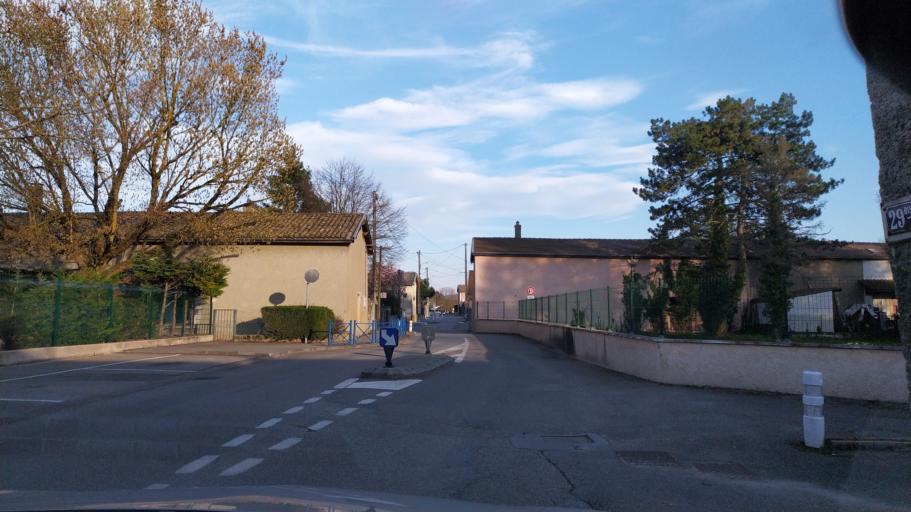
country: FR
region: Rhone-Alpes
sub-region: Departement de l'Isere
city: Charvieu-Chavagneux
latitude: 45.7271
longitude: 5.1472
